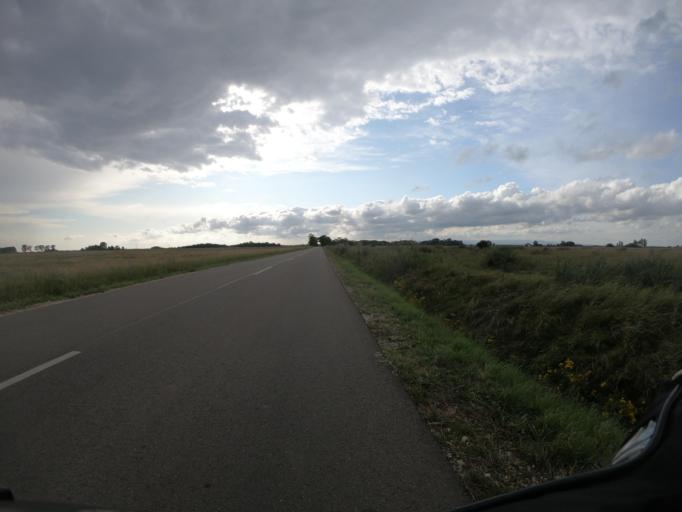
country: HU
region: Borsod-Abauj-Zemplen
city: Mezocsat
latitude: 47.8203
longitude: 20.8595
